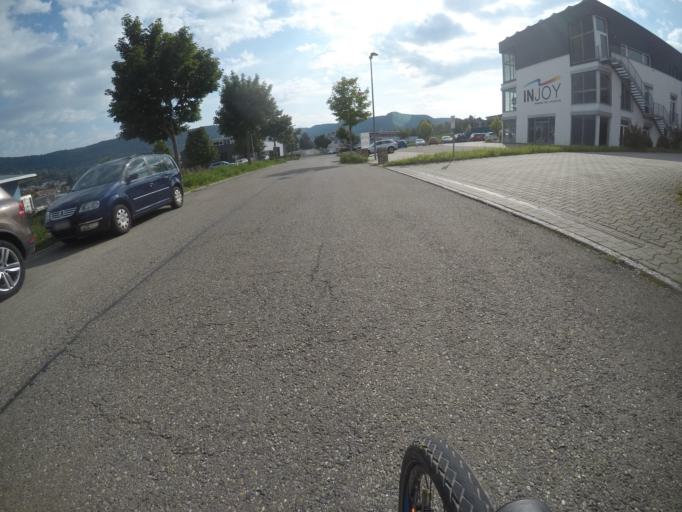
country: DE
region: Baden-Wuerttemberg
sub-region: Tuebingen Region
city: Dettingen an der Erms
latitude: 48.5282
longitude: 9.3377
